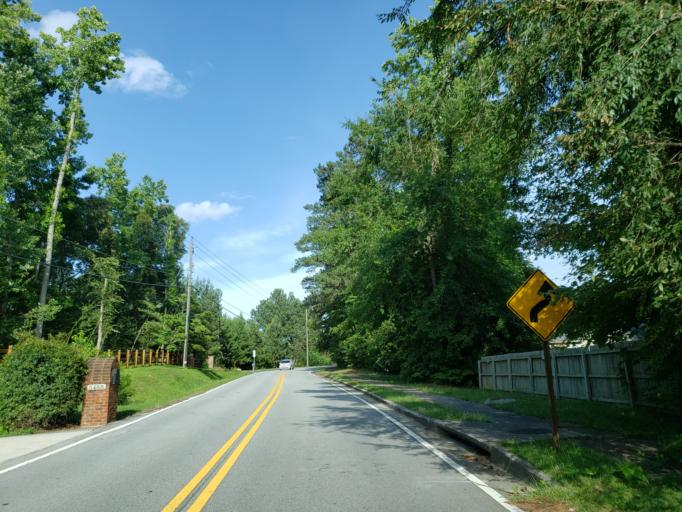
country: US
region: Georgia
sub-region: Cobb County
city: Powder Springs
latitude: 33.9123
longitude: -84.7110
